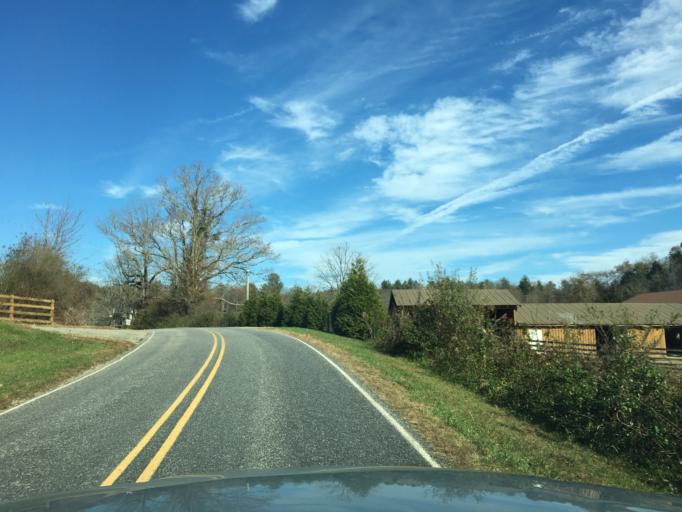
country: US
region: North Carolina
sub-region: Henderson County
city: Etowah
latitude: 35.3081
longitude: -82.6258
